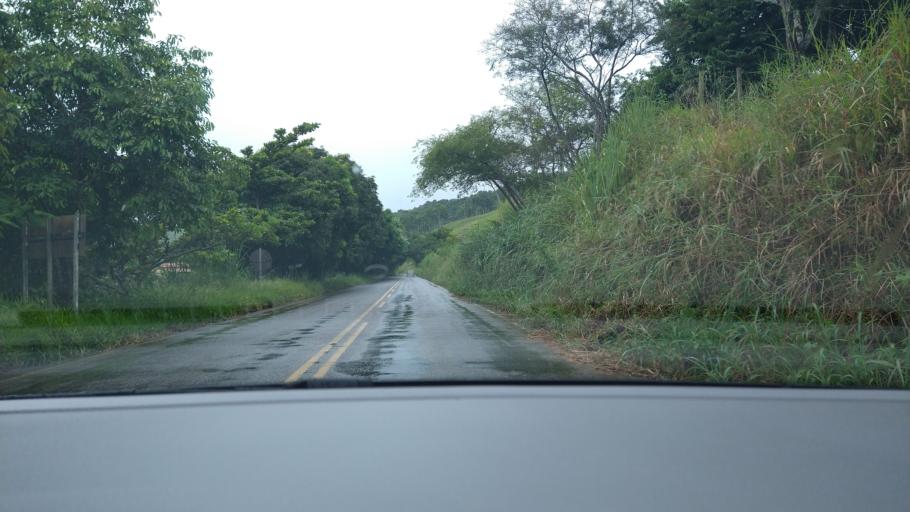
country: BR
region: Minas Gerais
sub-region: Ponte Nova
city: Ponte Nova
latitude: -20.3774
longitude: -42.8996
